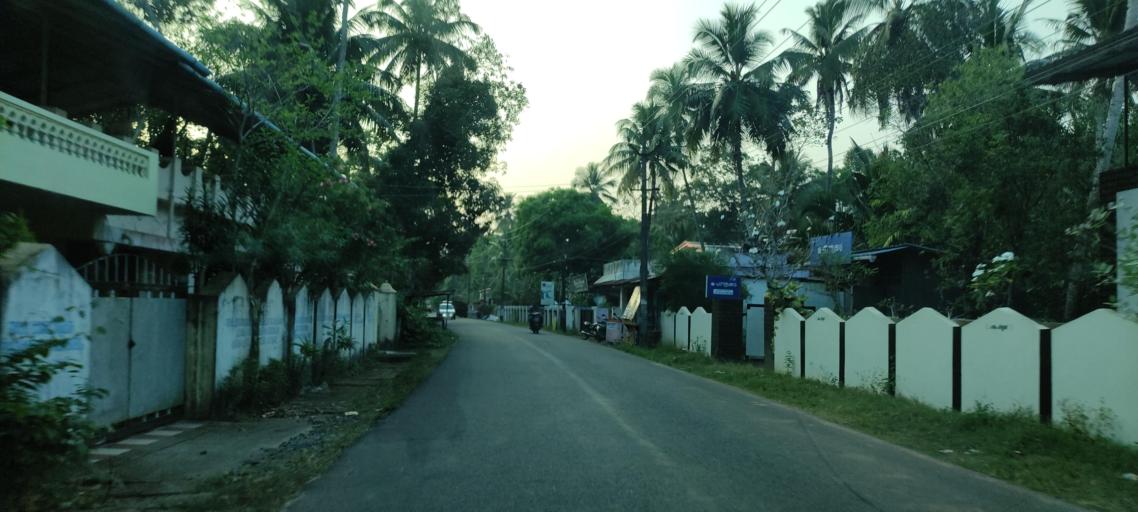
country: IN
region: Kerala
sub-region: Alappuzha
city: Kayankulam
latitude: 9.1354
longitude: 76.5342
